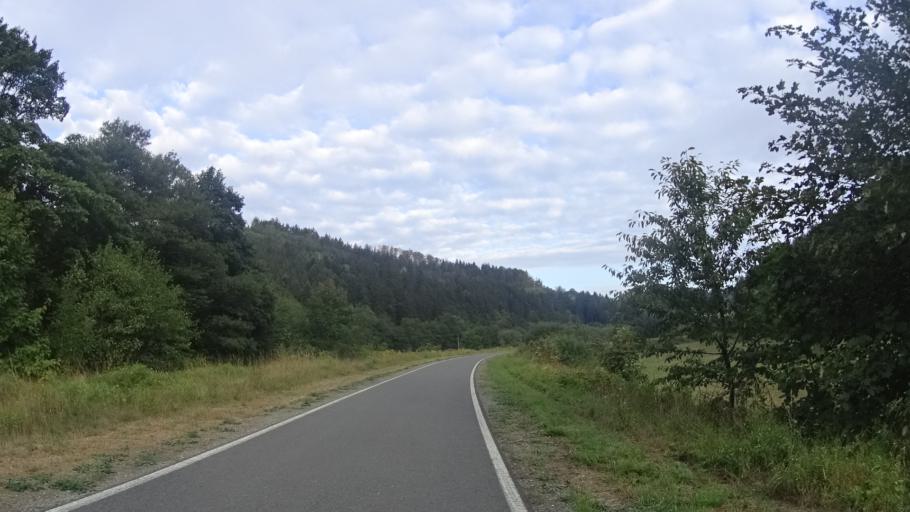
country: CZ
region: Olomoucky
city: Zabreh
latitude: 49.8586
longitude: 16.8244
